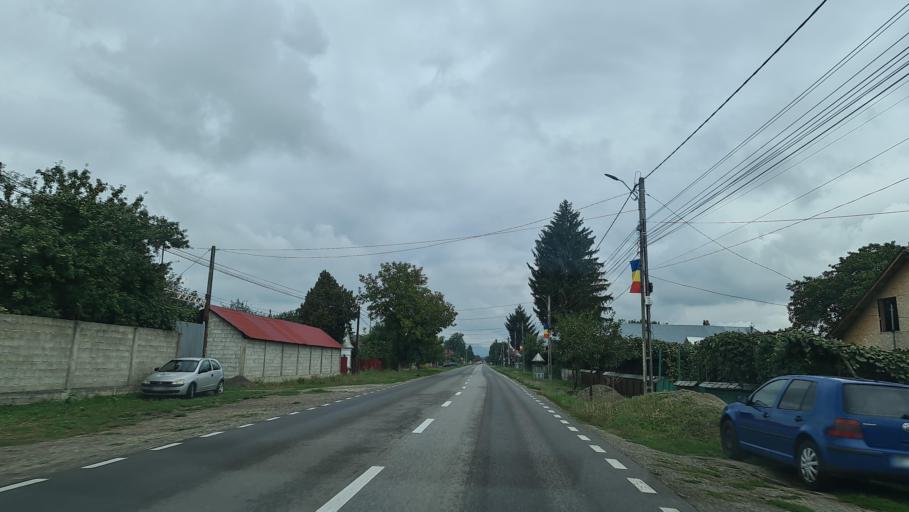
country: RO
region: Neamt
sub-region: Comuna Roznov
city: Roznov
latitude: 46.8109
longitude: 26.5173
